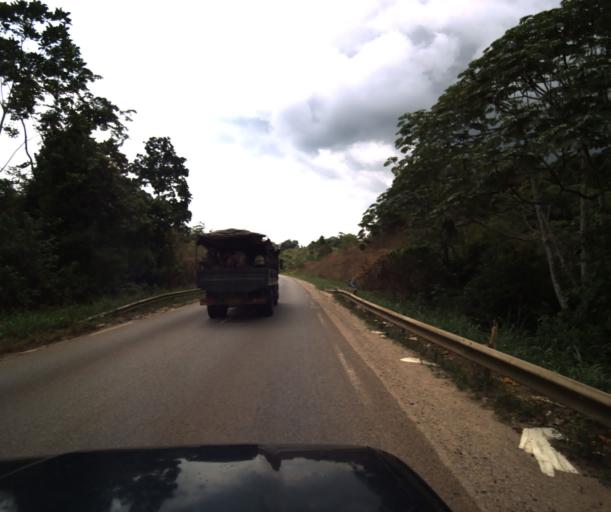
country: CM
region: Littoral
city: Dizangue
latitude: 3.9506
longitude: 10.0152
